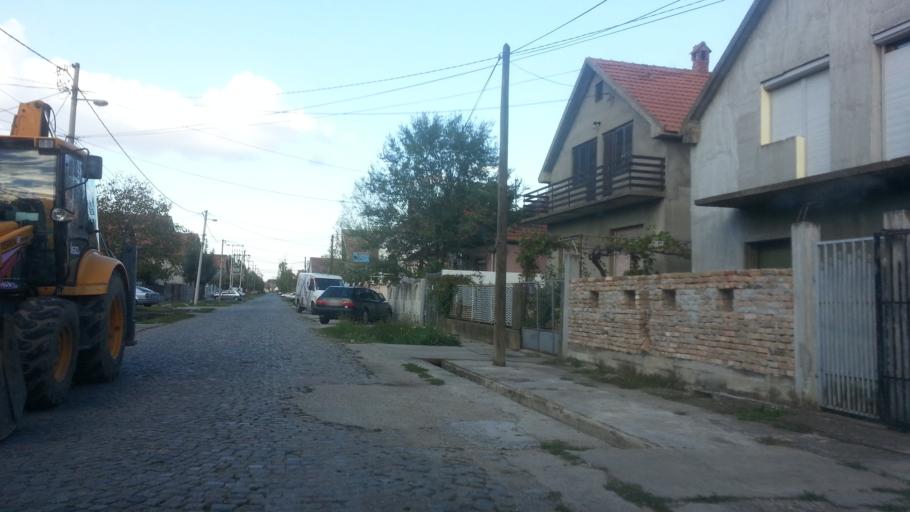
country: RS
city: Novi Banovci
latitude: 44.9085
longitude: 20.2618
